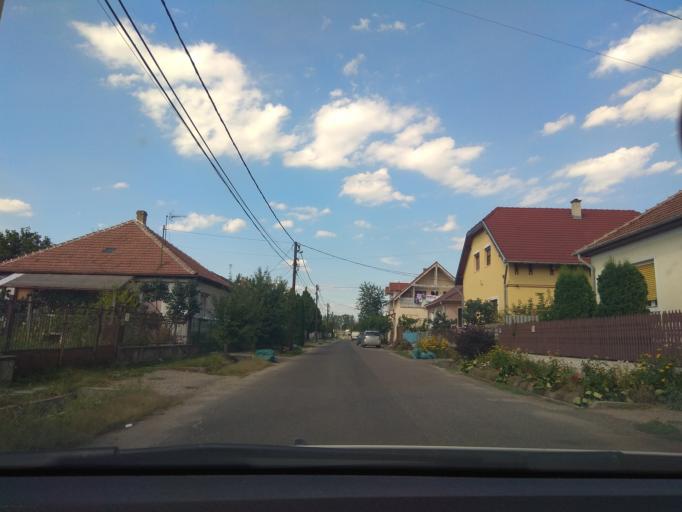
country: HU
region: Borsod-Abauj-Zemplen
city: Miskolc
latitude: 48.0560
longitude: 20.7943
